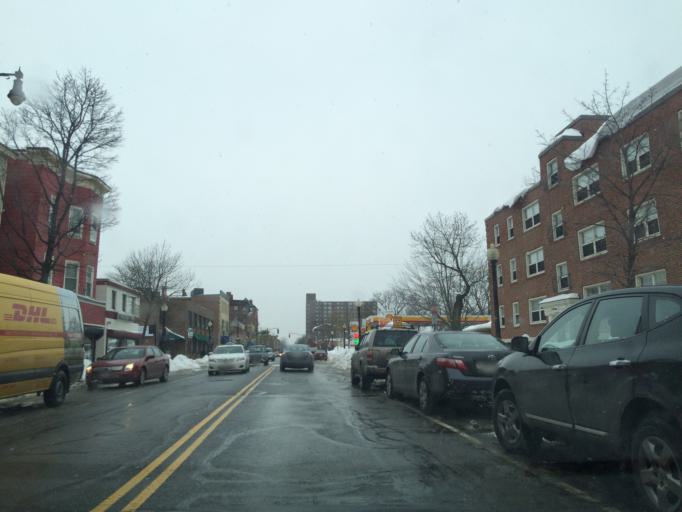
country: US
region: Massachusetts
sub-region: Middlesex County
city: Cambridge
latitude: 42.3727
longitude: -71.0925
